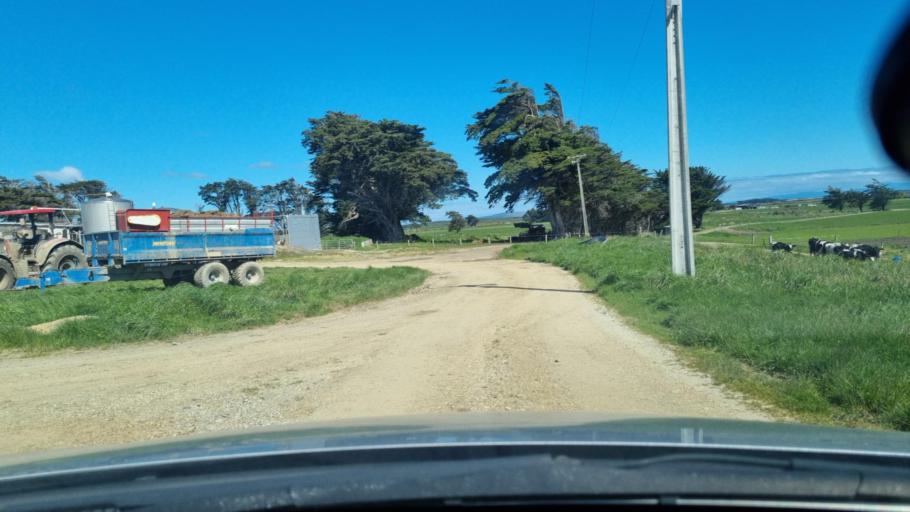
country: NZ
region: Southland
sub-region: Invercargill City
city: Invercargill
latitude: -46.4009
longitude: 168.2561
